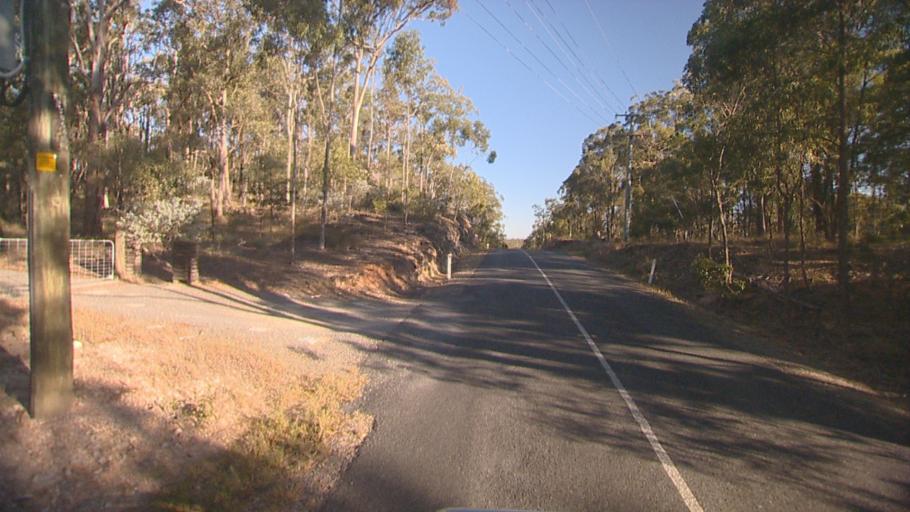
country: AU
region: Queensland
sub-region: Logan
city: Chambers Flat
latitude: -27.7633
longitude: 153.1229
